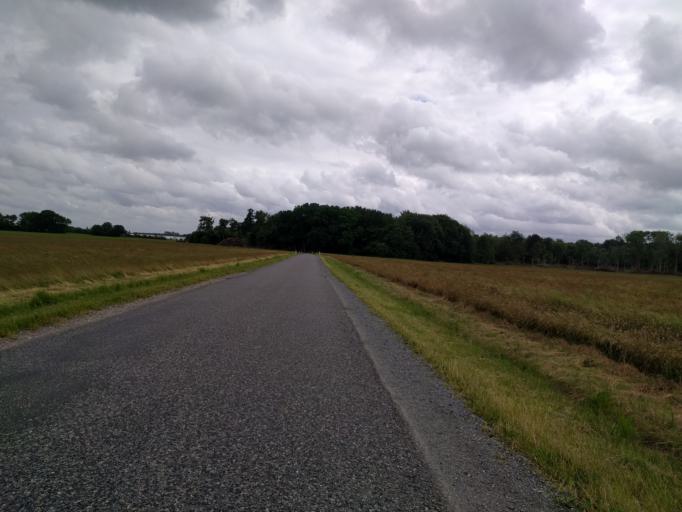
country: DK
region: South Denmark
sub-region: Kerteminde Kommune
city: Munkebo
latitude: 55.4179
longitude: 10.5342
